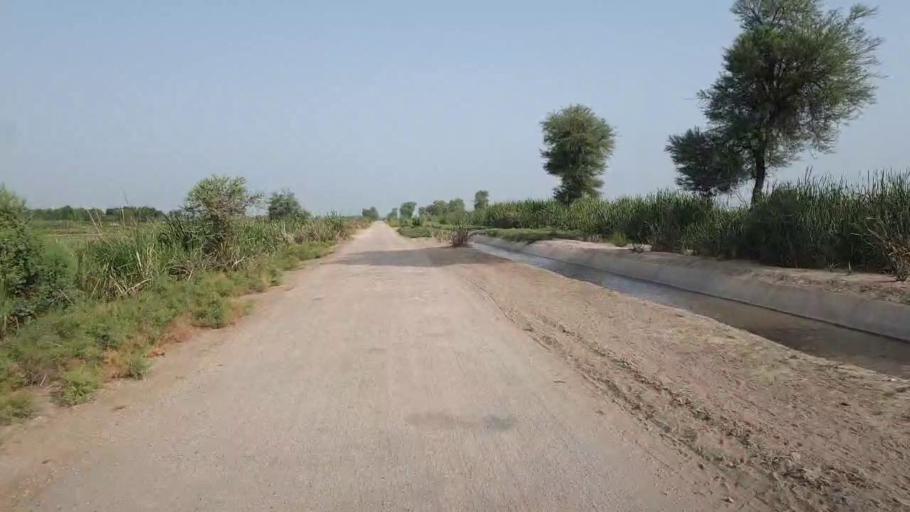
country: PK
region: Sindh
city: Daur
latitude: 26.3396
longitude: 68.1829
